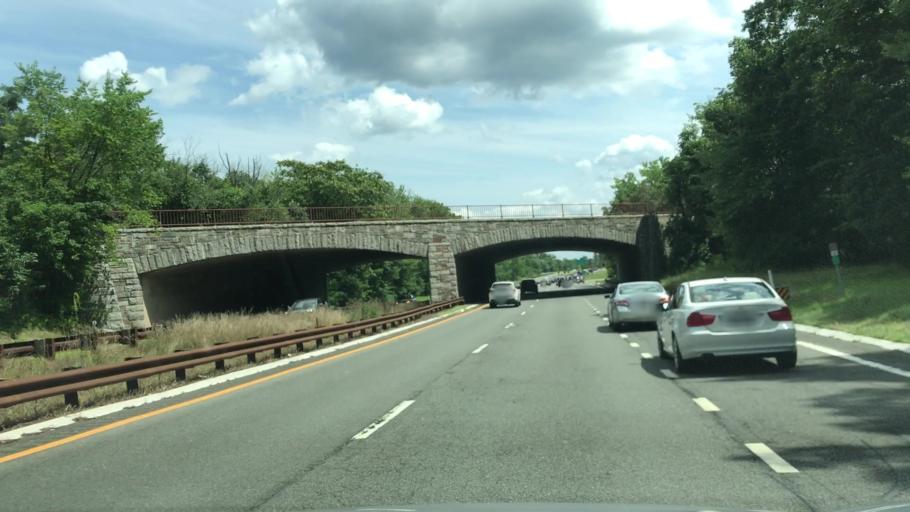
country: US
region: New York
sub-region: Rockland County
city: Bardonia
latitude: 41.1070
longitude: -73.9970
